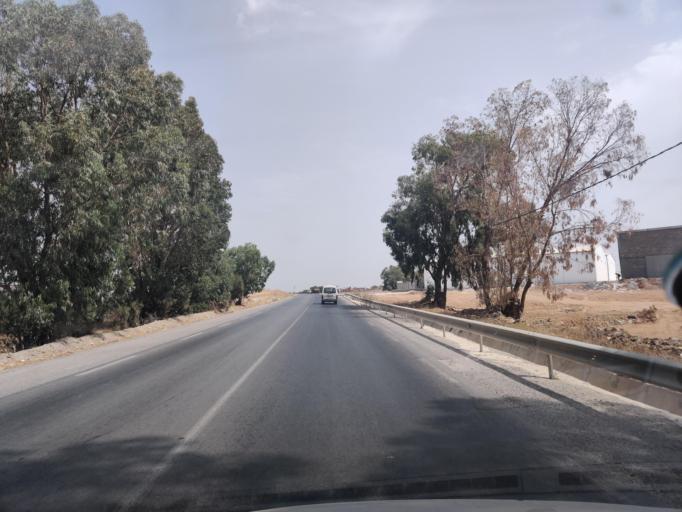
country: TN
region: Nabul
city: Bu `Urqub
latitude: 36.4644
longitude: 10.5715
